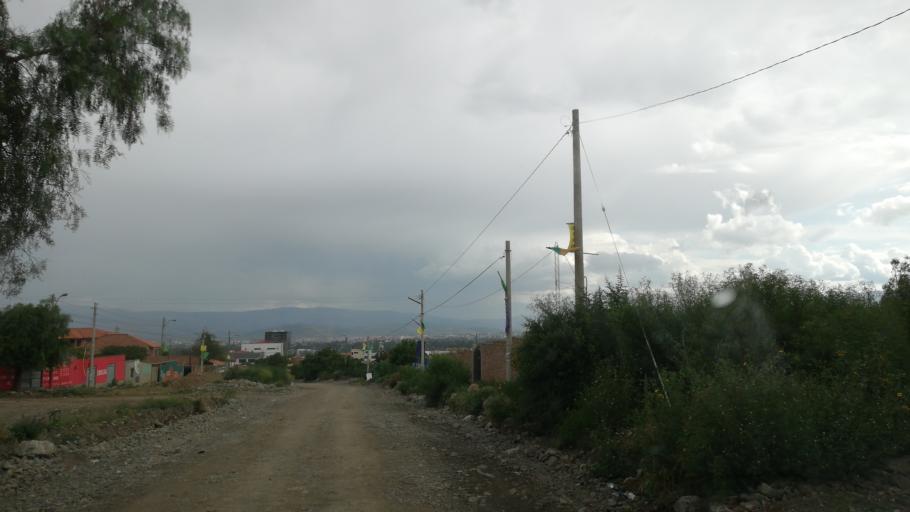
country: BO
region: Cochabamba
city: Cochabamba
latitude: -17.3389
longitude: -66.1986
